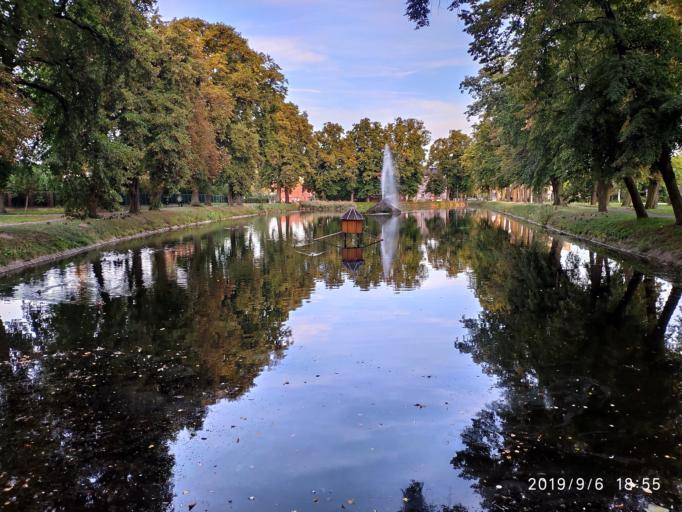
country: PL
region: Lubusz
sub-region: Powiat wschowski
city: Wschowa
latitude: 51.8038
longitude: 16.3096
